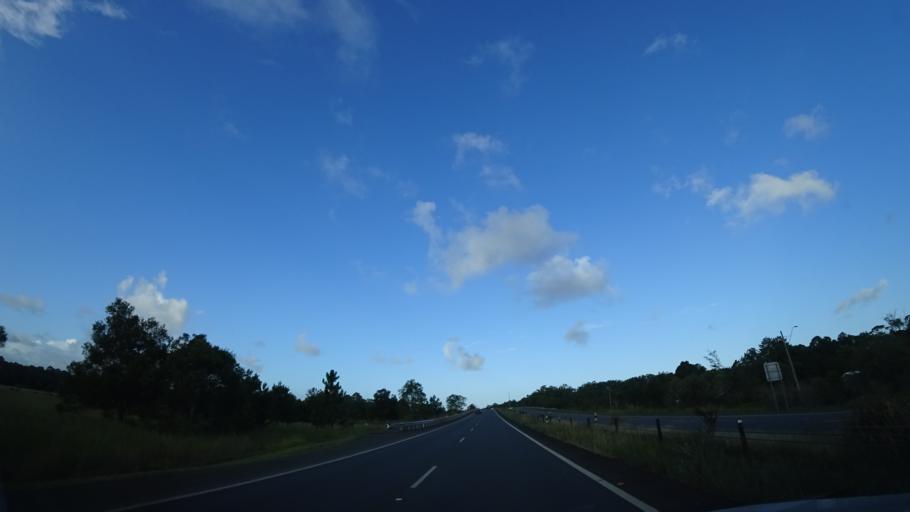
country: AU
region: Queensland
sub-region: Sunshine Coast
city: Buderim
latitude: -26.6696
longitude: 153.0194
